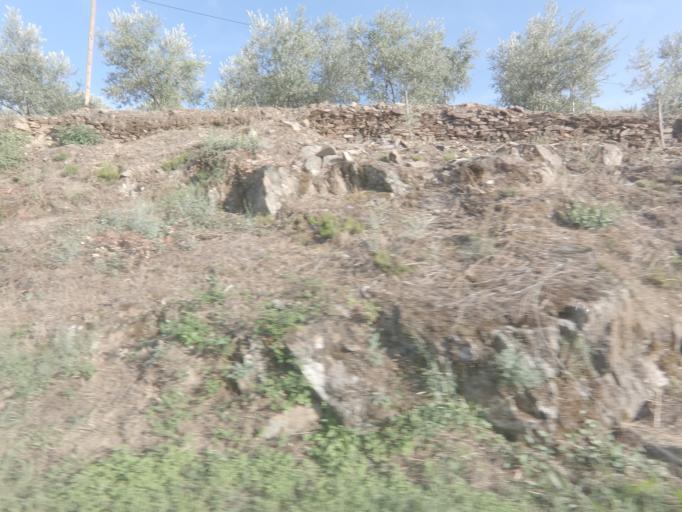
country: PT
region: Vila Real
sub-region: Sabrosa
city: Sabrosa
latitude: 41.2260
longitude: -7.5256
